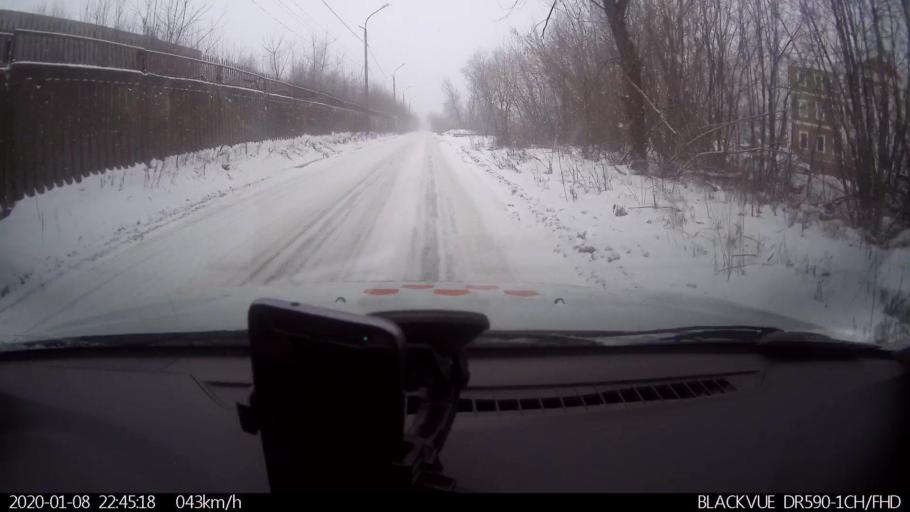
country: RU
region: Nizjnij Novgorod
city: Nizhniy Novgorod
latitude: 56.2994
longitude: 43.9037
